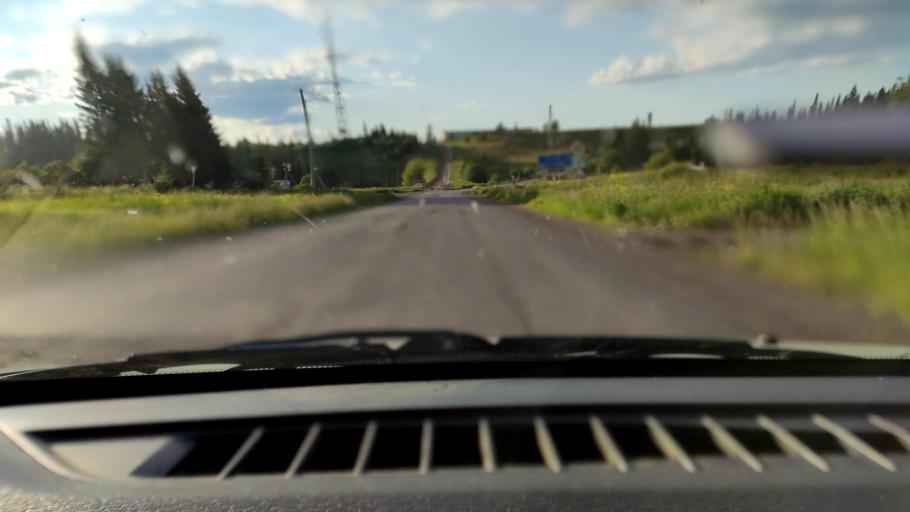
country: RU
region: Perm
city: Uinskoye
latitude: 57.1078
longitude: 56.5323
